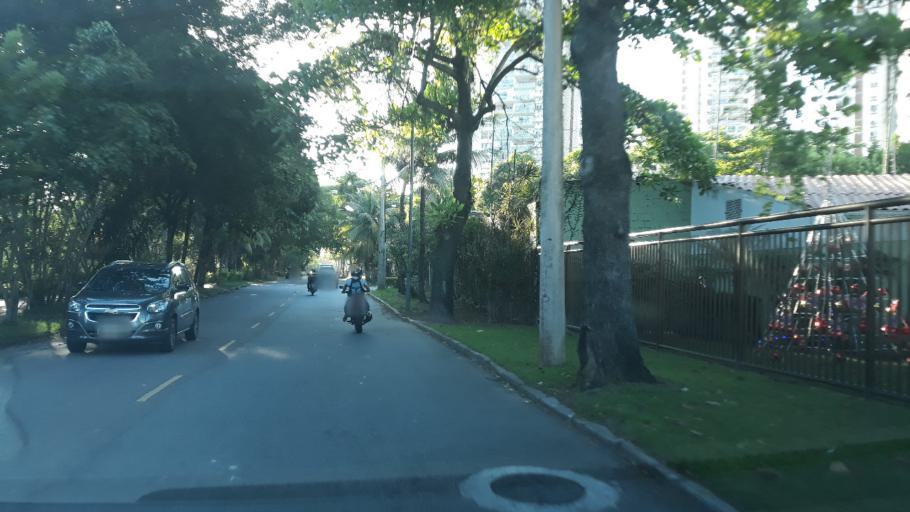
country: BR
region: Rio de Janeiro
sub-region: Rio De Janeiro
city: Rio de Janeiro
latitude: -23.0061
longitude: -43.3380
